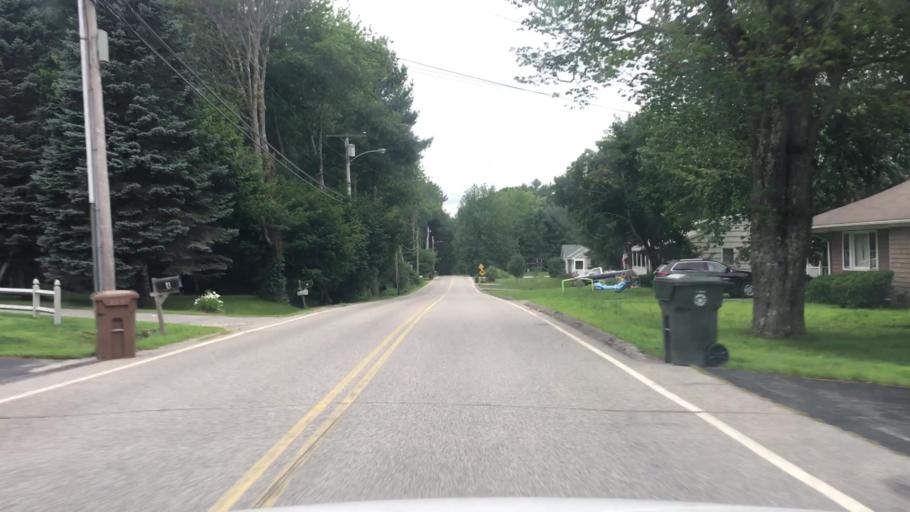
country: US
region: Maine
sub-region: York County
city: Biddeford
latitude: 43.5025
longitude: -70.4682
